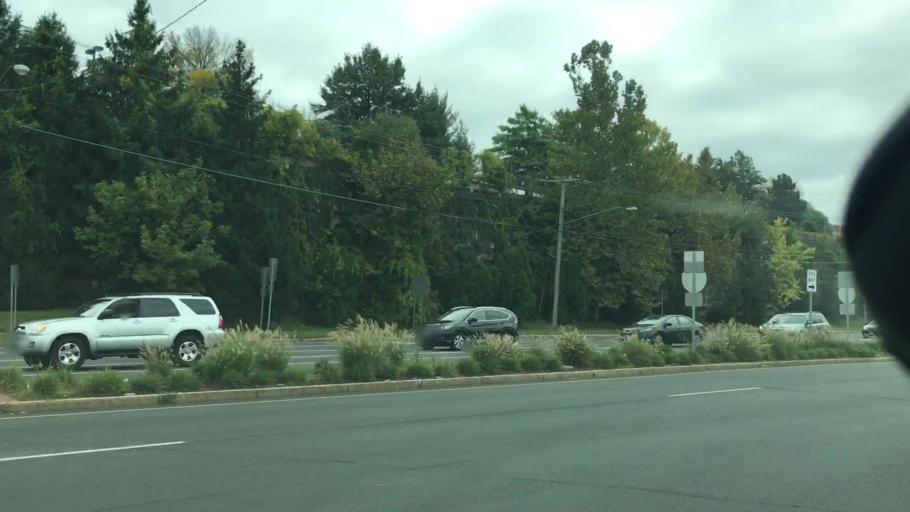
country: US
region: Connecticut
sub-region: Hartford County
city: Manchester
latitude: 41.8060
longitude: -72.5550
